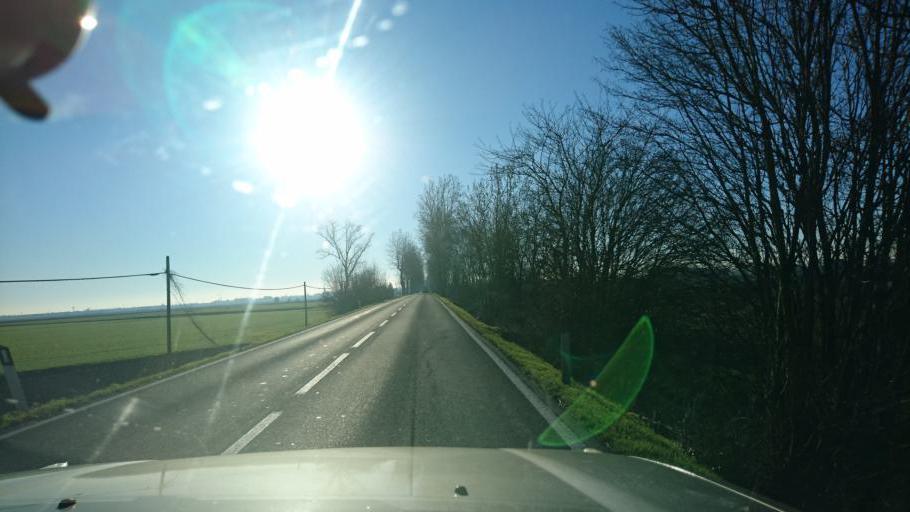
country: IT
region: Veneto
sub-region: Provincia di Venezia
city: Rottanova
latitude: 45.1576
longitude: 12.0532
